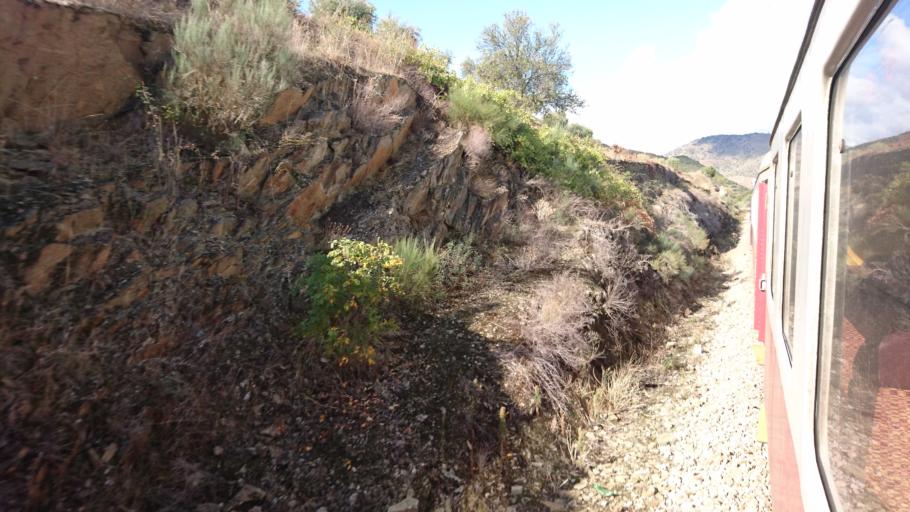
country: PT
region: Guarda
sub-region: Vila Nova de Foz Coa
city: Vila Nova de Foz Coa
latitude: 41.1379
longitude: -7.2334
